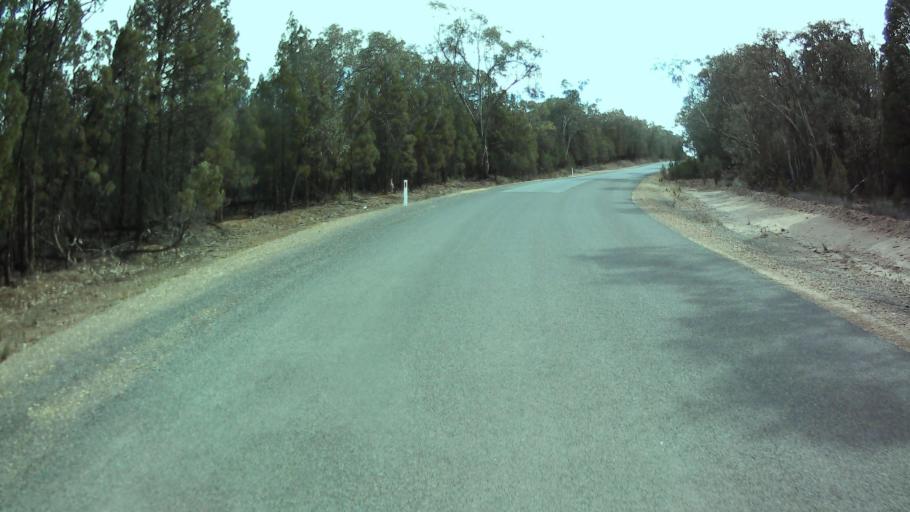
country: AU
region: New South Wales
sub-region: Weddin
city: Grenfell
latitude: -33.8960
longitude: 148.1857
